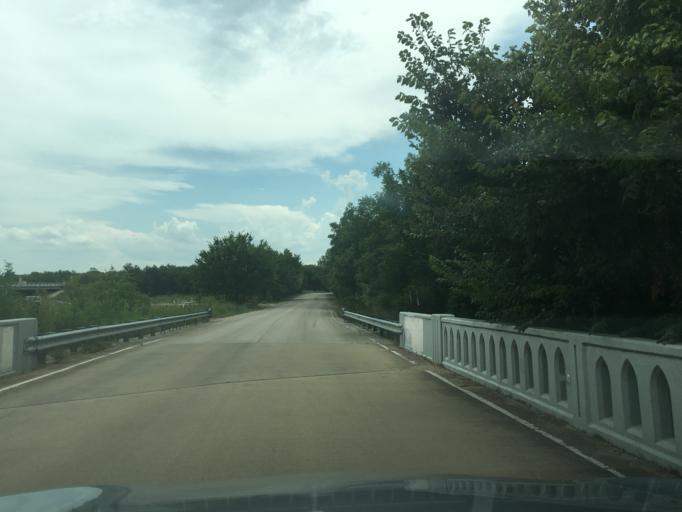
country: US
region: Texas
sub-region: Denton County
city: Denton
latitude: 33.1785
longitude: -97.1635
